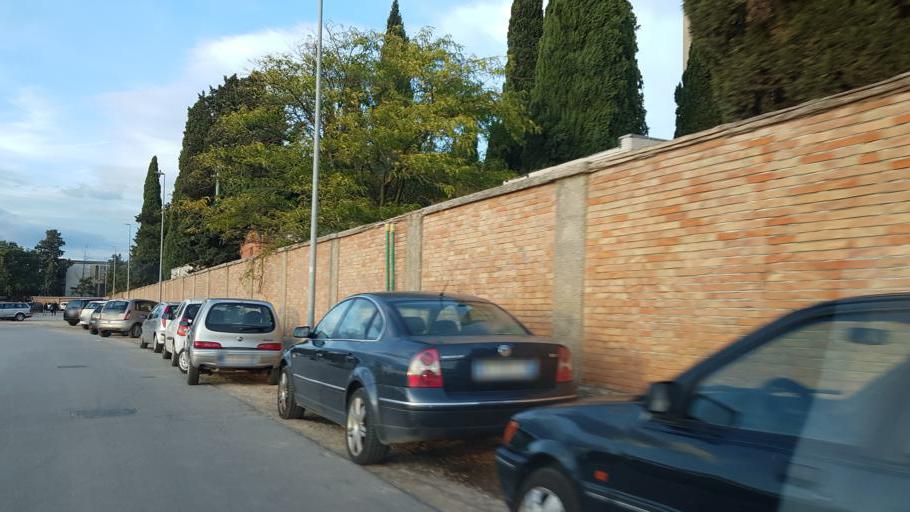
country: IT
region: Apulia
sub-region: Provincia di Foggia
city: Foggia
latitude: 41.4752
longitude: 15.5471
